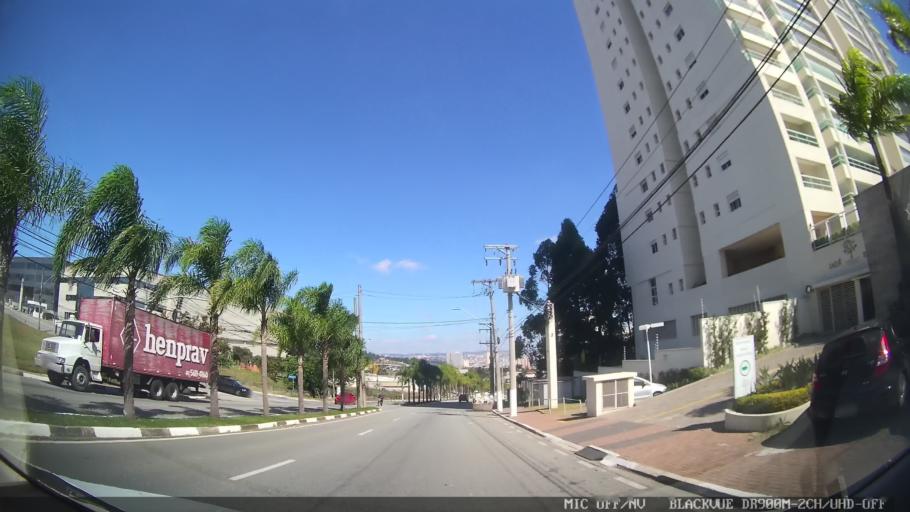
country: BR
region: Sao Paulo
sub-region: Carapicuiba
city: Carapicuiba
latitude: -23.4740
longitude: -46.8306
